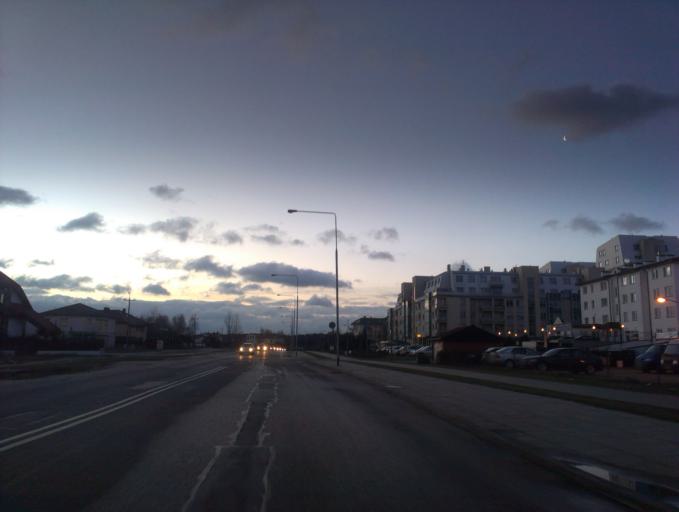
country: PL
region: Masovian Voivodeship
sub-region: Warszawa
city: Kabaty
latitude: 52.1325
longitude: 21.0760
